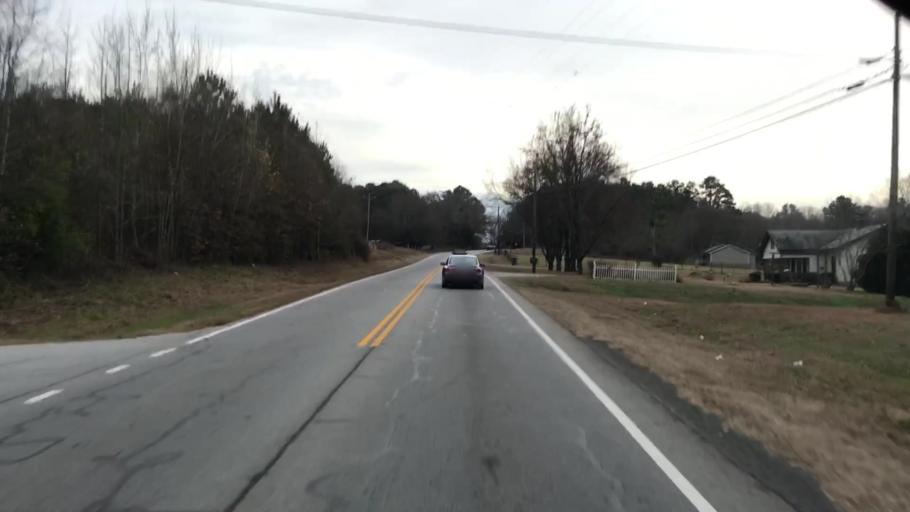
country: US
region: Georgia
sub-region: Barrow County
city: Auburn
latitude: 34.0337
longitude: -83.7741
